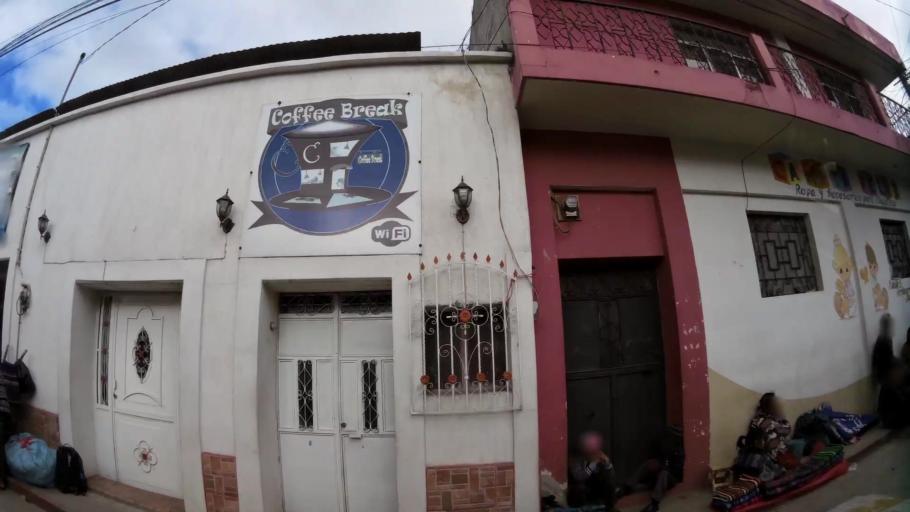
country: GT
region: Quetzaltenango
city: Salcaja
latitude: 14.8785
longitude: -91.4589
